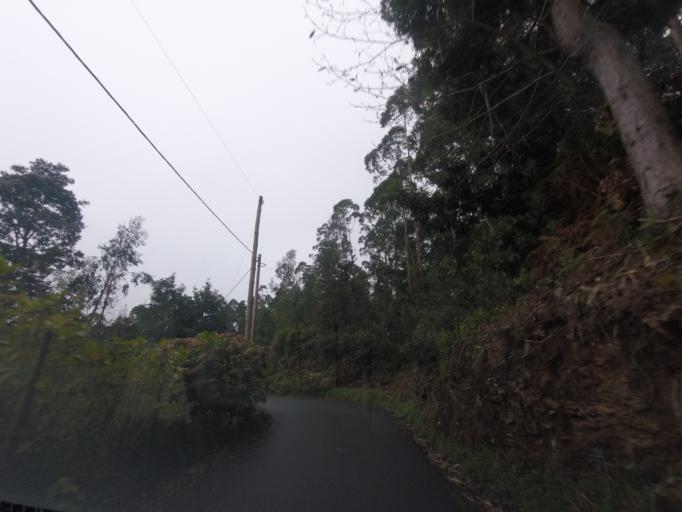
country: PT
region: Madeira
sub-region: Santana
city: Santana
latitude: 32.7864
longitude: -16.8975
